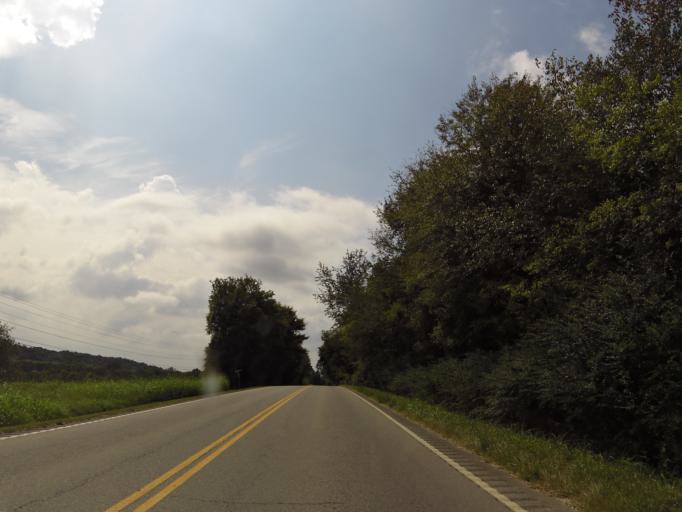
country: US
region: Tennessee
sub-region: Perry County
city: Linden
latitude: 35.6874
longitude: -87.8043
